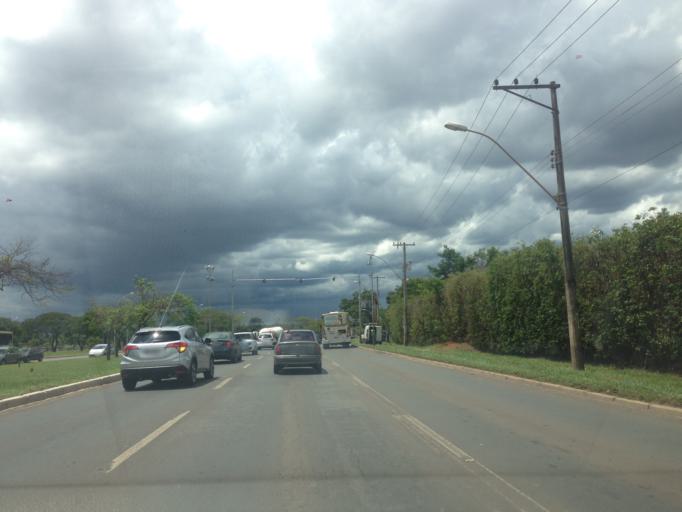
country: BR
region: Federal District
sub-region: Brasilia
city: Brasilia
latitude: -15.8235
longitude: -47.9348
